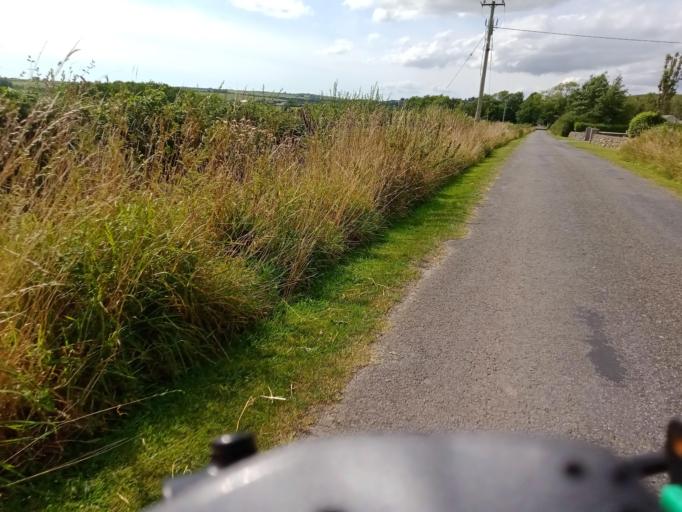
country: IE
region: Munster
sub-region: Waterford
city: Dungarvan
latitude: 52.1403
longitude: -7.4933
